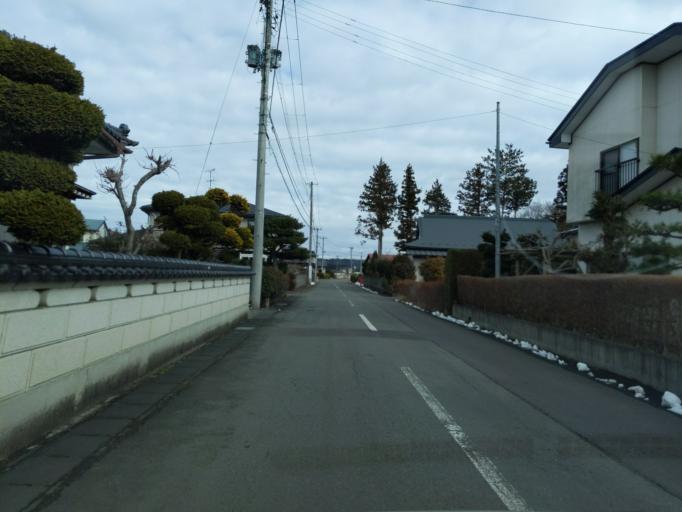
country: JP
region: Iwate
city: Mizusawa
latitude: 39.0882
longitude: 141.1736
